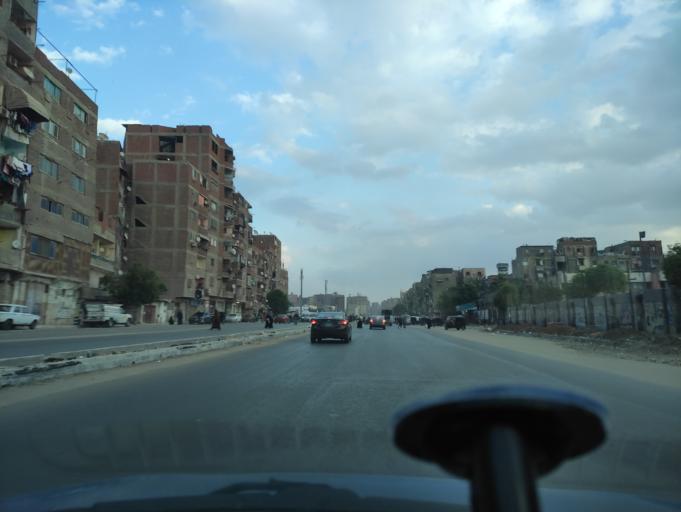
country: EG
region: Muhafazat al Qalyubiyah
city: Al Khankah
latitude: 30.1373
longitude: 31.3493
